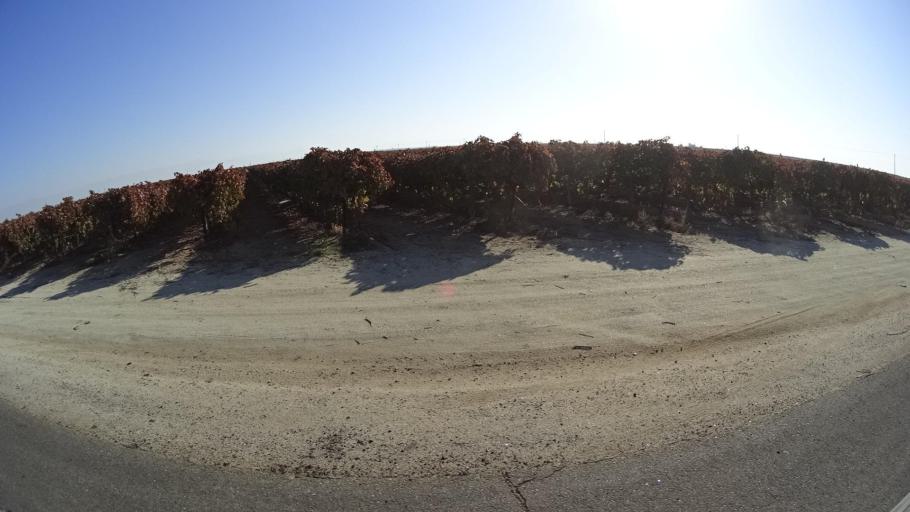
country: US
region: California
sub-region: Tulare County
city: Richgrove
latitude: 35.7344
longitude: -119.1495
